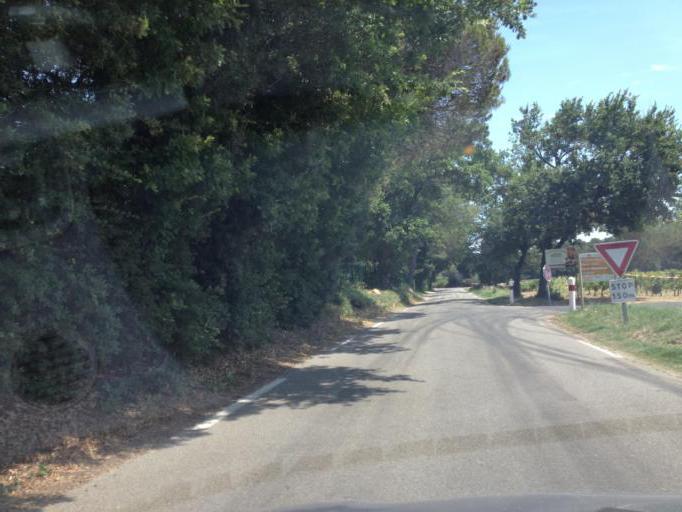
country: FR
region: Provence-Alpes-Cote d'Azur
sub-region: Departement du Vaucluse
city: Uchaux
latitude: 44.2113
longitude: 4.7995
